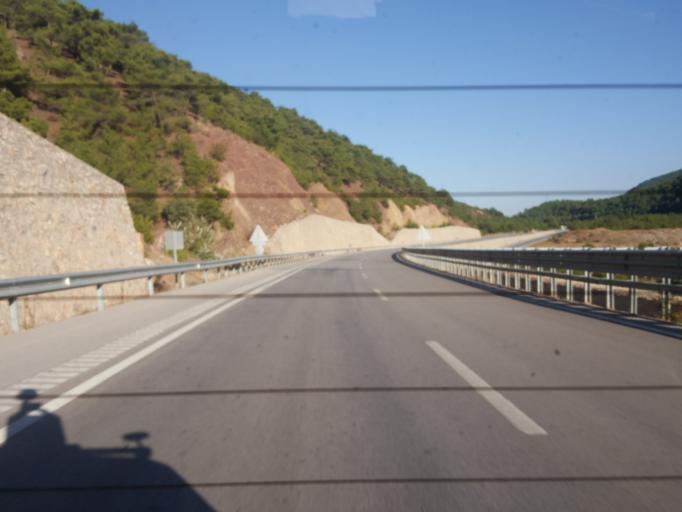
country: TR
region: Amasya
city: Akdag
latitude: 40.7543
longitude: 36.0684
